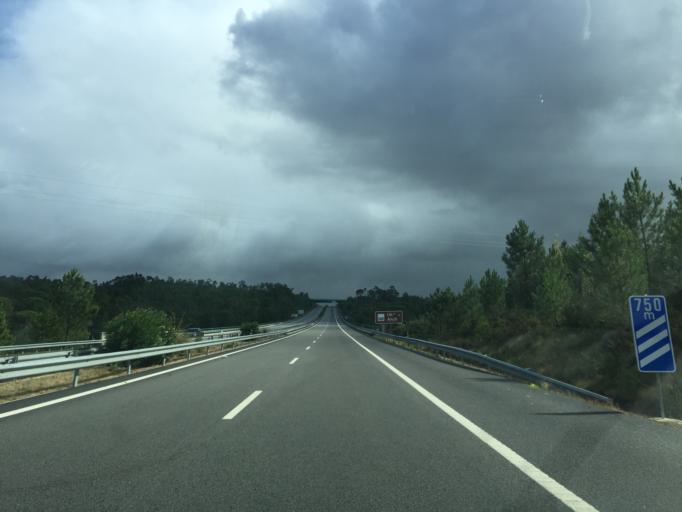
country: PT
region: Coimbra
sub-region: Cantanhede
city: Cantanhede
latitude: 40.2839
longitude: -8.5405
